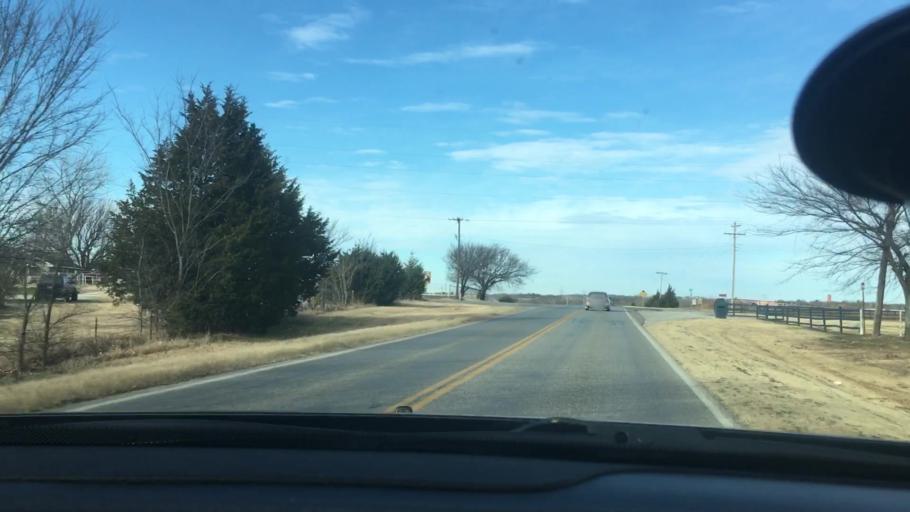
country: US
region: Oklahoma
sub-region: Seminole County
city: Konawa
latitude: 34.9487
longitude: -96.7391
